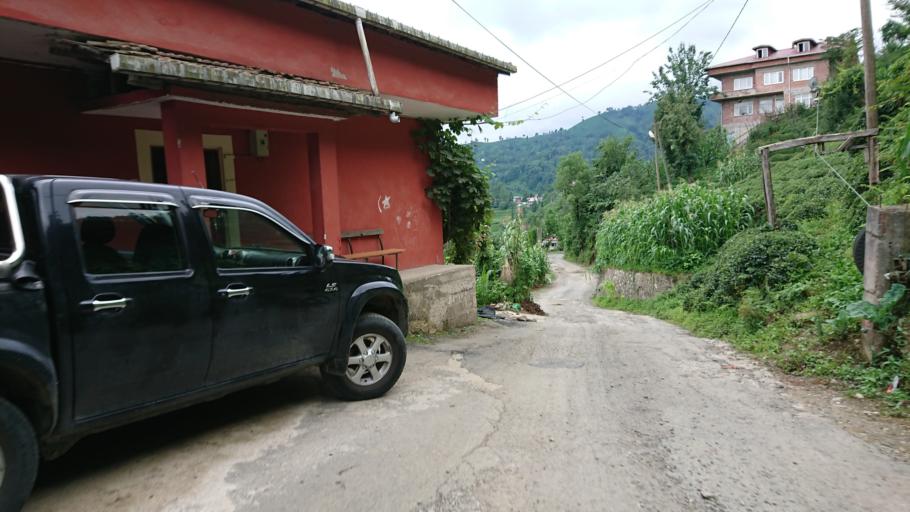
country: TR
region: Rize
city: Rize
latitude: 40.9686
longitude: 40.5132
